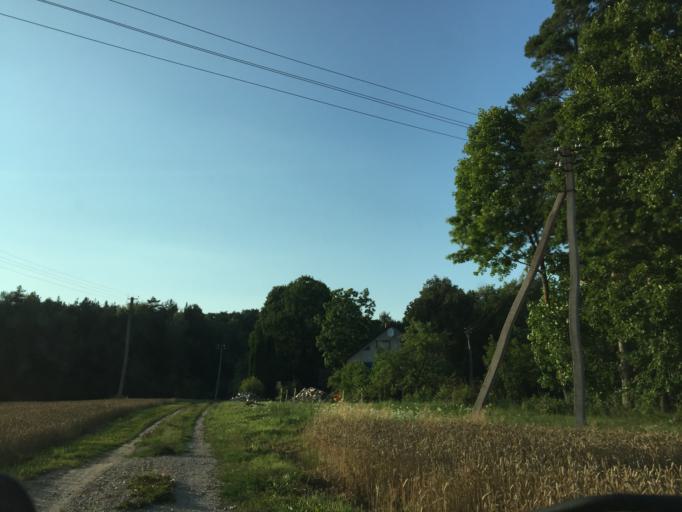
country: LV
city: Tervete
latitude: 56.4722
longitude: 23.3758
